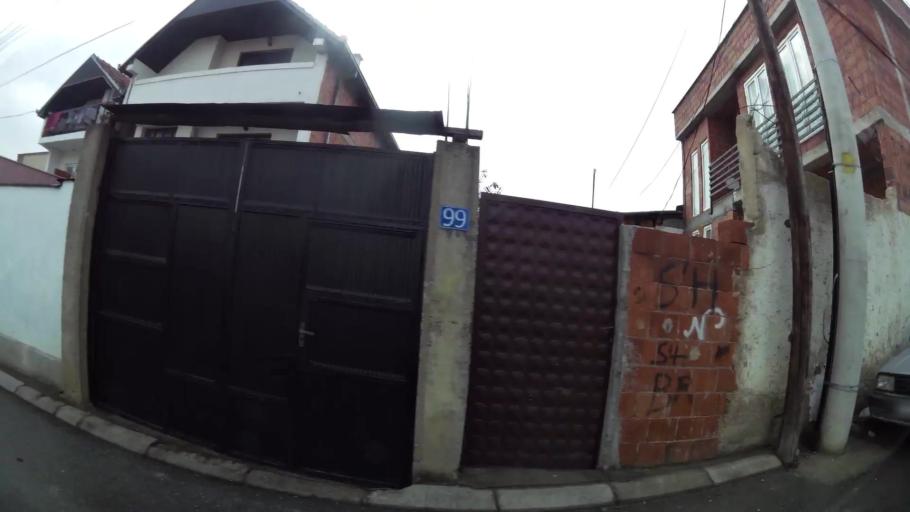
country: XK
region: Pristina
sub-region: Komuna e Prishtines
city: Pristina
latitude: 42.6731
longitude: 21.1596
